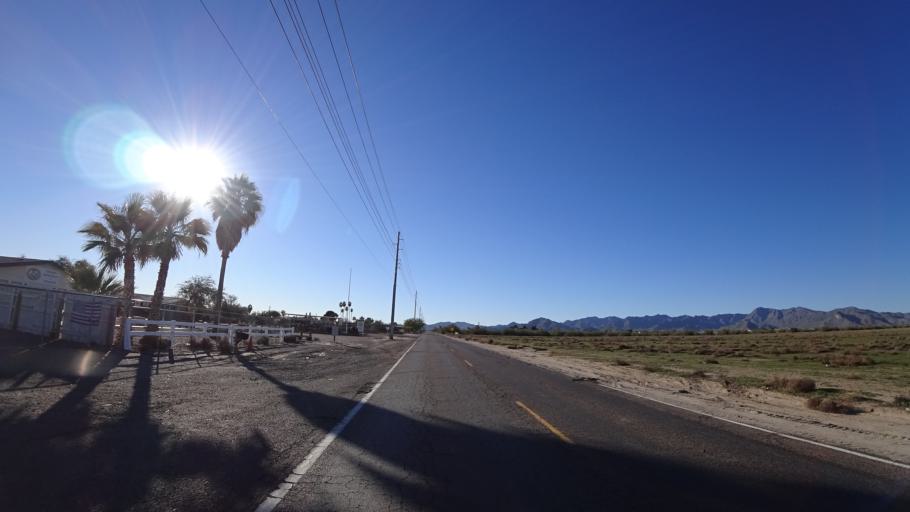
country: US
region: Arizona
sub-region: Maricopa County
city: Citrus Park
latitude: 33.4646
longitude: -112.4664
